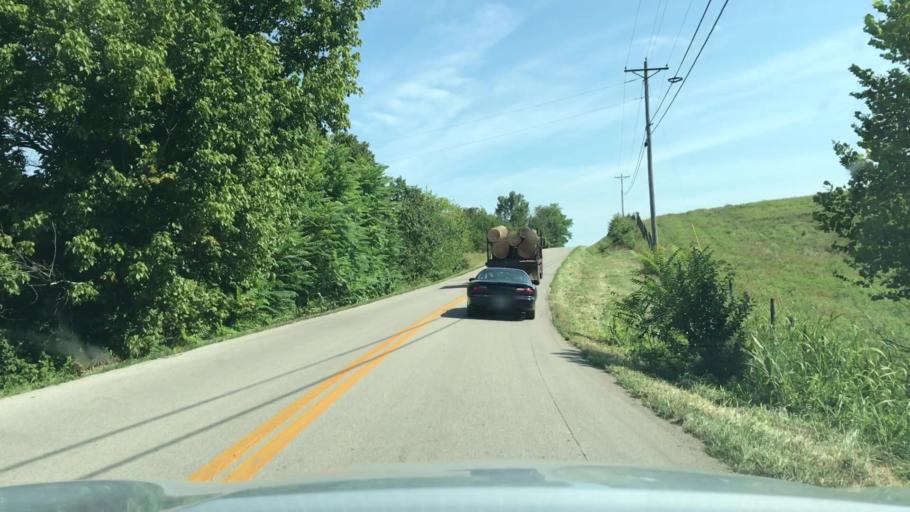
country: US
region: Kentucky
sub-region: Clinton County
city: Albany
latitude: 36.7586
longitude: -84.9980
